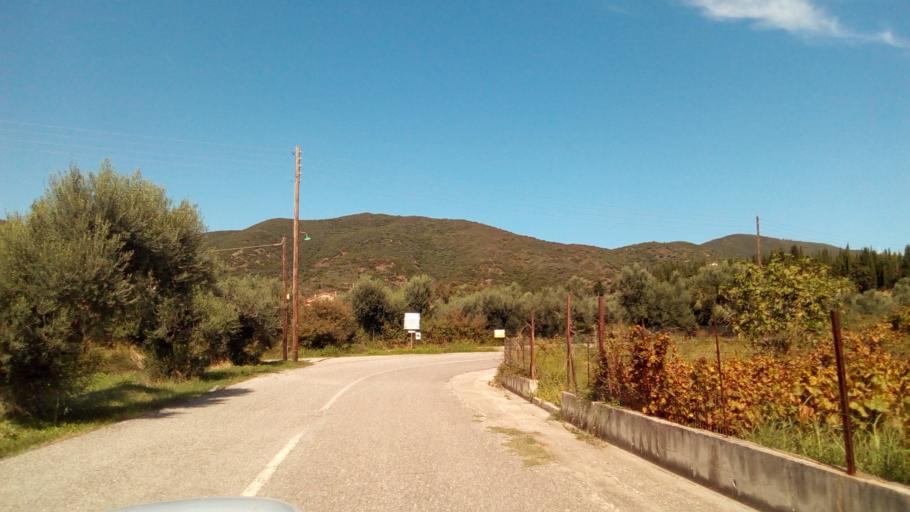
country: GR
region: West Greece
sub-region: Nomos Aitolias kai Akarnanias
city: Antirrio
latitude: 38.3550
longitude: 21.7542
